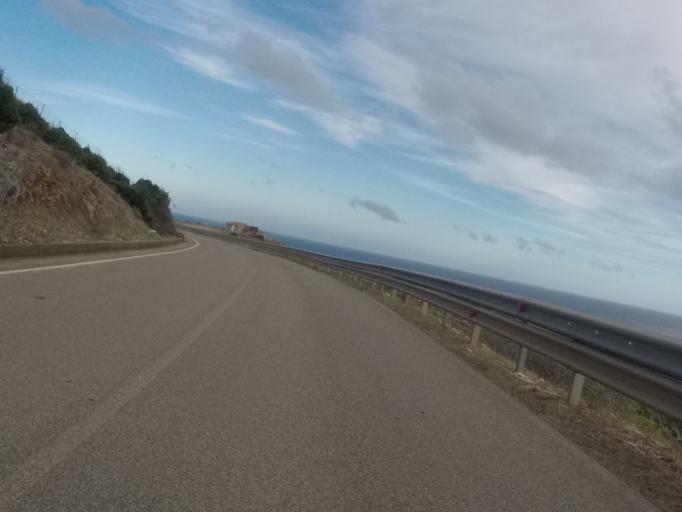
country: IT
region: Sardinia
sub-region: Provincia di Carbonia-Iglesias
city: Buggerru
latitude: 39.3954
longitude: 8.3991
